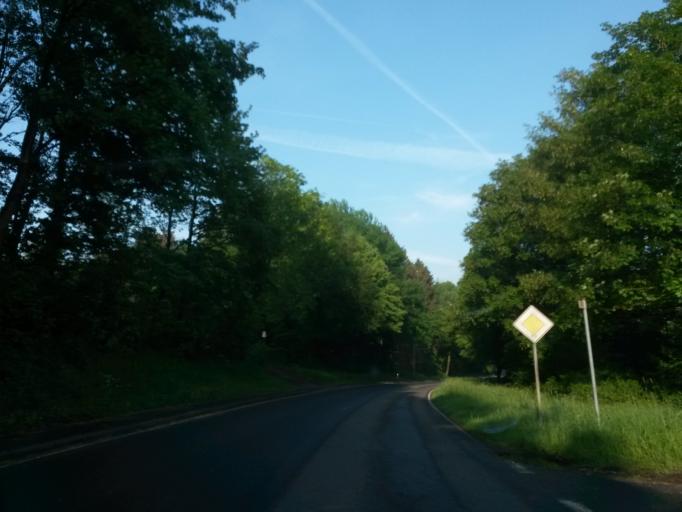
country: DE
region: North Rhine-Westphalia
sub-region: Regierungsbezirk Koln
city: Much
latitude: 50.9427
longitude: 7.4470
